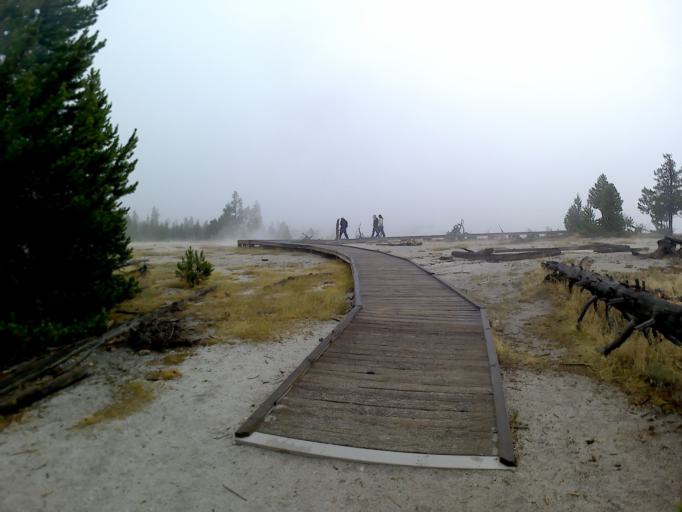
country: US
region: Montana
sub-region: Gallatin County
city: West Yellowstone
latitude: 44.4856
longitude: -110.8579
